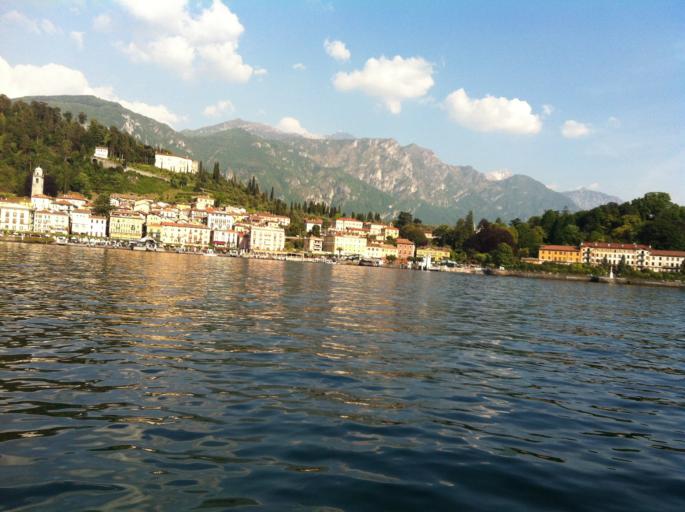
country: IT
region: Lombardy
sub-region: Provincia di Como
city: Bellagio
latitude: 45.9877
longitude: 9.2551
